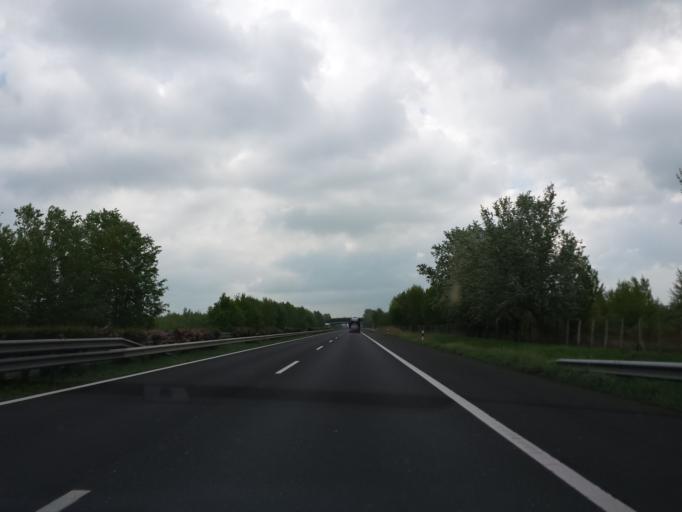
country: HU
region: Gyor-Moson-Sopron
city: Kimle
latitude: 47.7812
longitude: 17.3481
